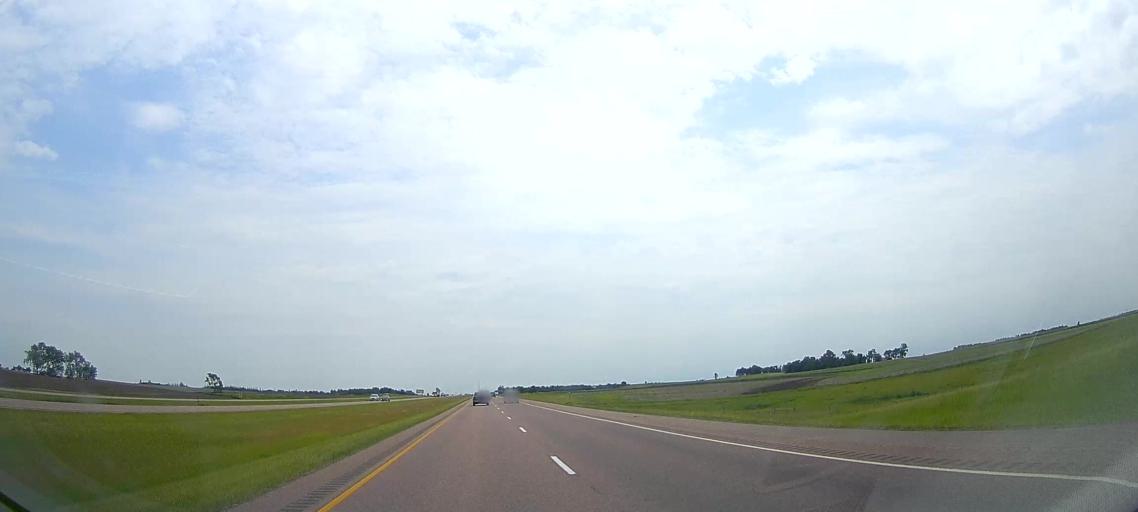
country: US
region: South Dakota
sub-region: Minnehaha County
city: Hartford
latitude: 43.6555
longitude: -97.1048
